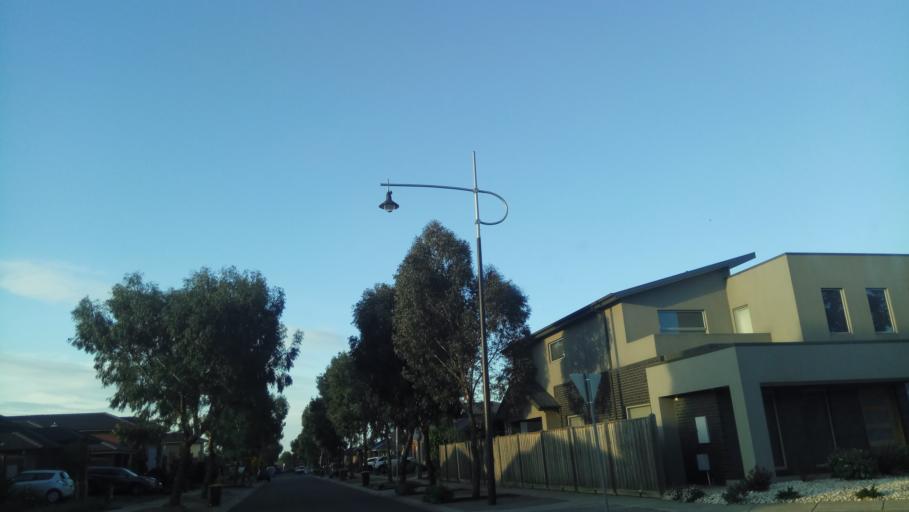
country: AU
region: Victoria
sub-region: Wyndham
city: Point Cook
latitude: -37.9008
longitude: 144.7366
